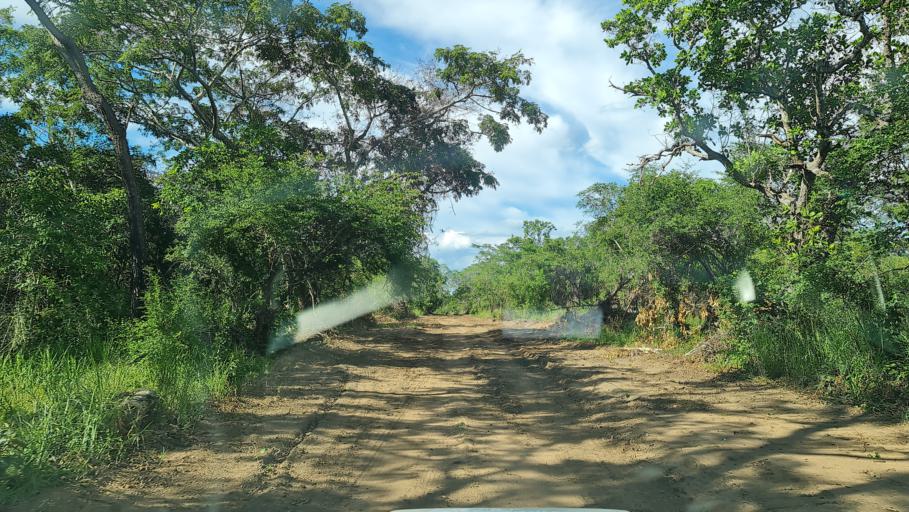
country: MZ
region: Nampula
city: Antonio Enes
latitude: -15.5229
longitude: 40.1277
